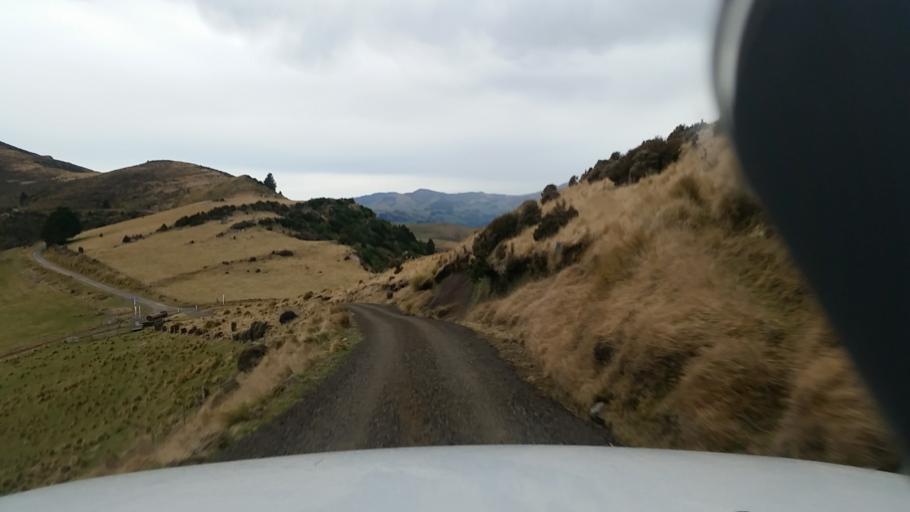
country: NZ
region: Canterbury
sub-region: Christchurch City
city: Christchurch
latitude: -43.8189
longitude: 172.8634
